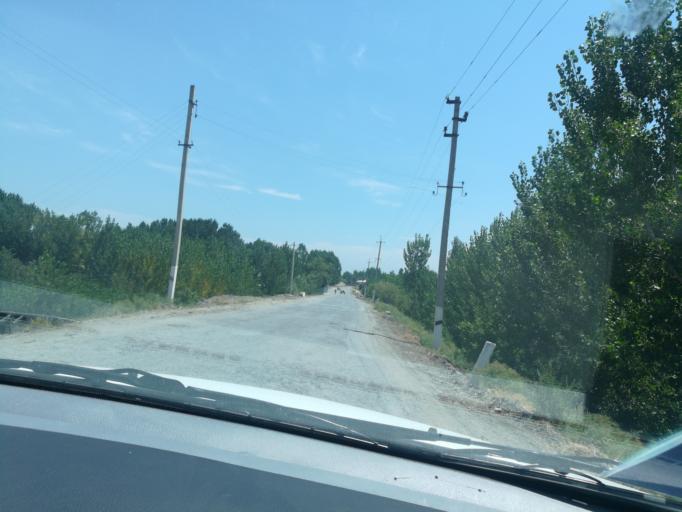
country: UZ
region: Namangan
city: Haqqulobod
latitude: 40.8988
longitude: 72.0043
